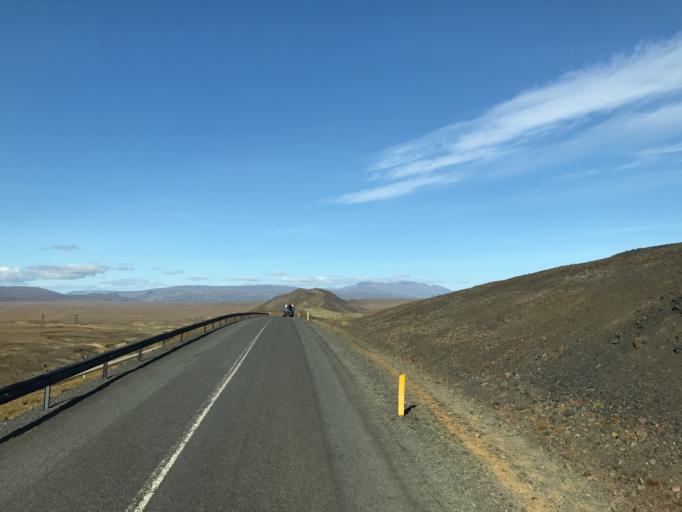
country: IS
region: South
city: Hveragerdi
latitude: 64.1203
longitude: -21.3163
